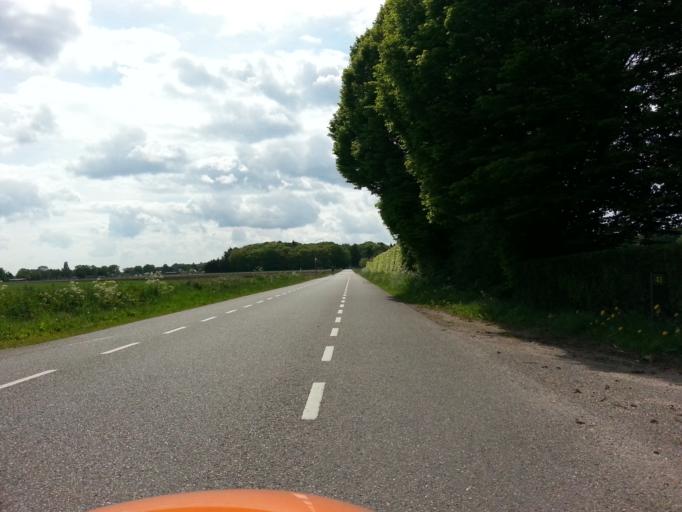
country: NL
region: Gelderland
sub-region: Gemeente Ede
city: Ede
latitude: 52.0742
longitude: 5.6780
